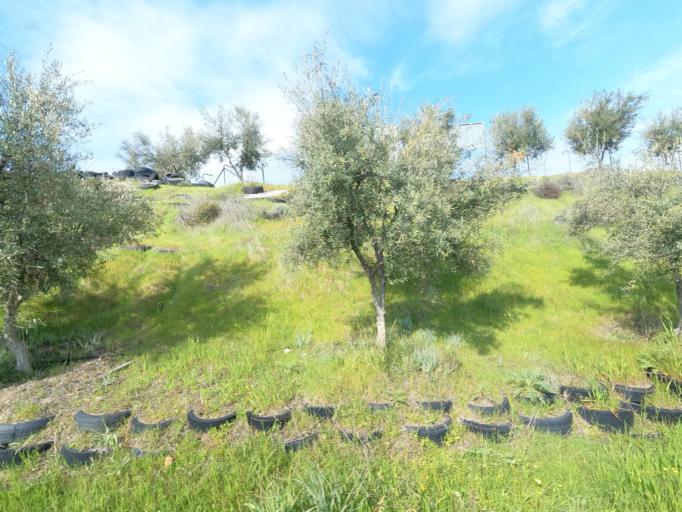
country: CY
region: Lefkosia
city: Astromeritis
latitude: 35.0822
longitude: 32.9539
